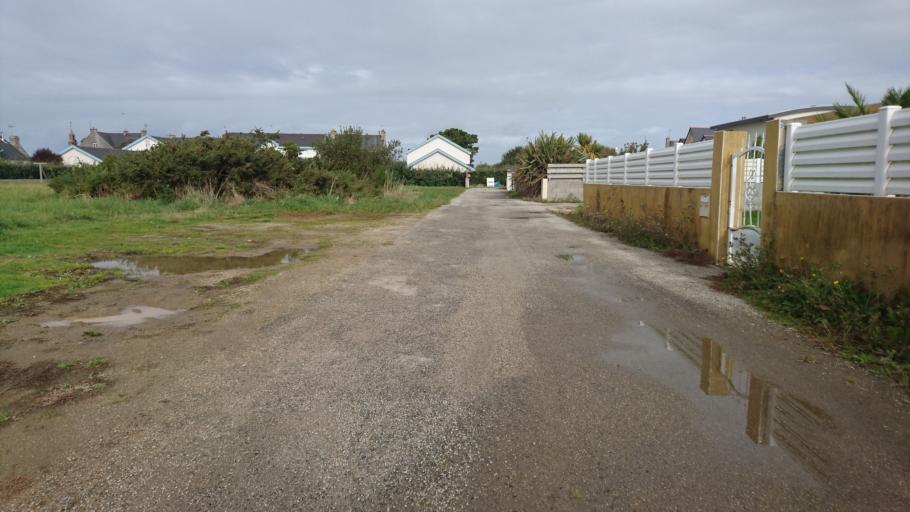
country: FR
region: Brittany
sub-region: Departement du Finistere
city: Lampaul-Plouarzel
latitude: 48.4460
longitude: -4.7590
